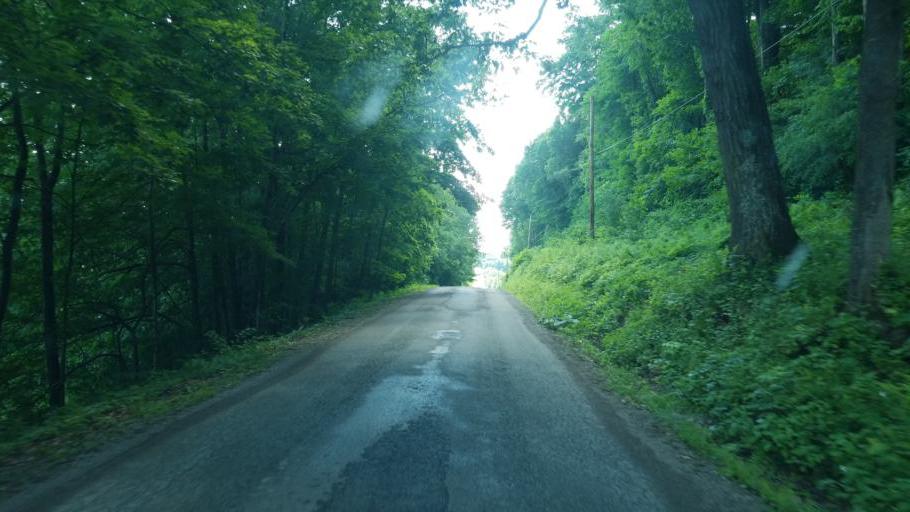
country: US
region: Ohio
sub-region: Knox County
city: Danville
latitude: 40.5123
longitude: -82.3235
